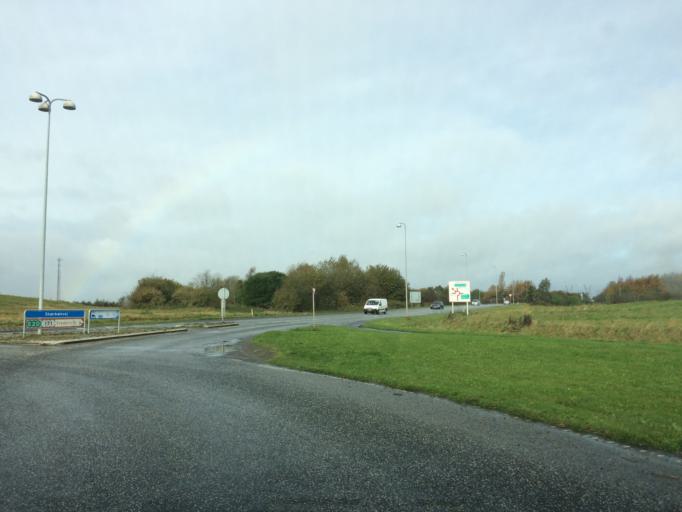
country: DK
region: South Denmark
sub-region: Fredericia Kommune
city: Taulov
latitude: 55.5355
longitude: 9.6381
